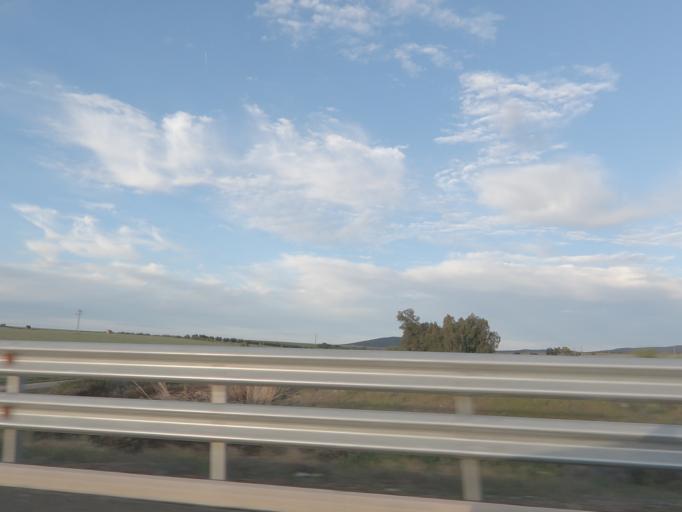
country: ES
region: Extremadura
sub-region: Provincia de Badajoz
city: Aljucen
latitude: 39.0248
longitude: -6.3328
